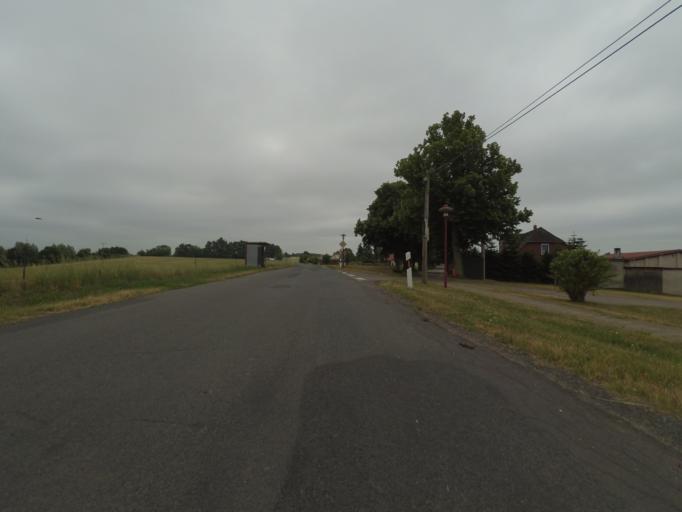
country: DE
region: Mecklenburg-Vorpommern
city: Sternberg
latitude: 53.6765
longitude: 11.8124
